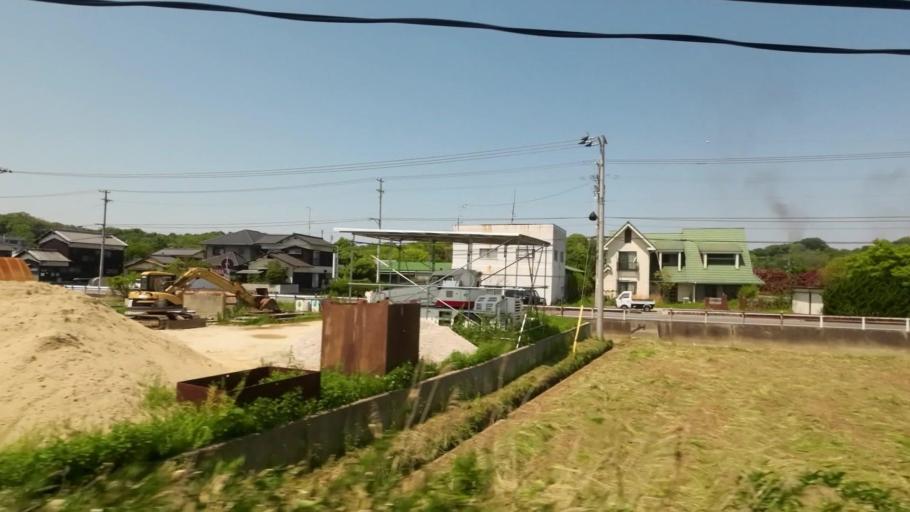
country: JP
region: Ehime
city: Hojo
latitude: 34.0786
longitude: 132.9310
